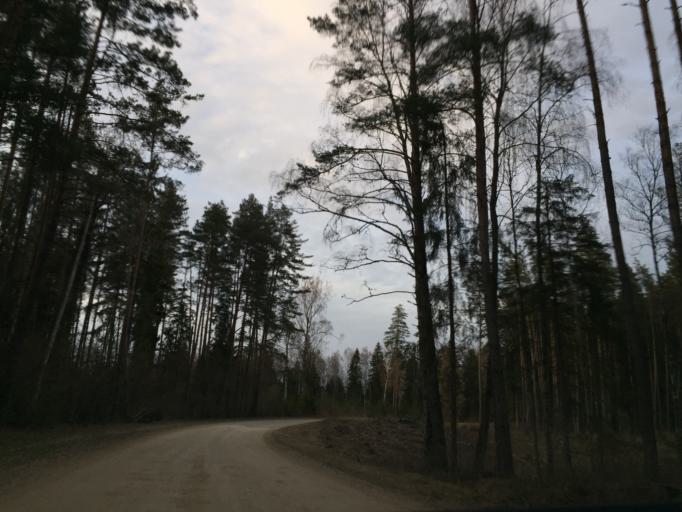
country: EE
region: Tartu
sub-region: UElenurme vald
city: Ulenurme
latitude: 58.2271
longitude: 26.6871
